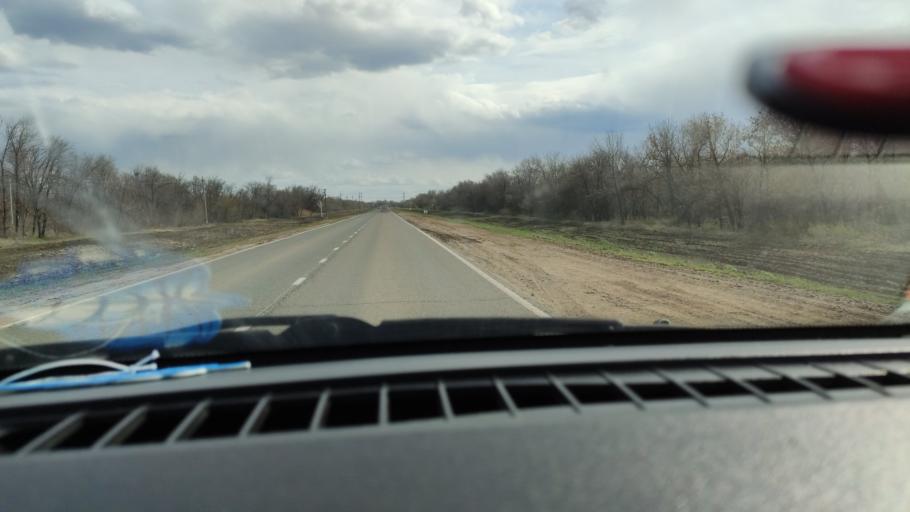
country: RU
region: Saratov
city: Privolzhskiy
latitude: 51.3752
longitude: 46.0447
